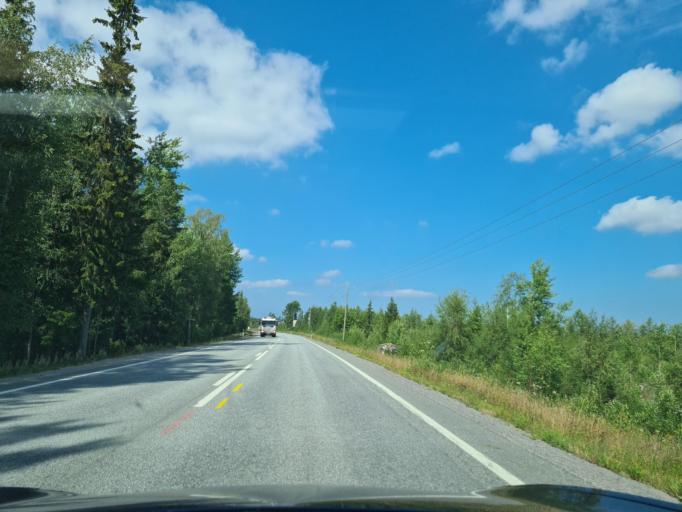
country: FI
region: Ostrobothnia
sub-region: Vaasa
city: Vaasa
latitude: 63.1646
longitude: 21.5903
